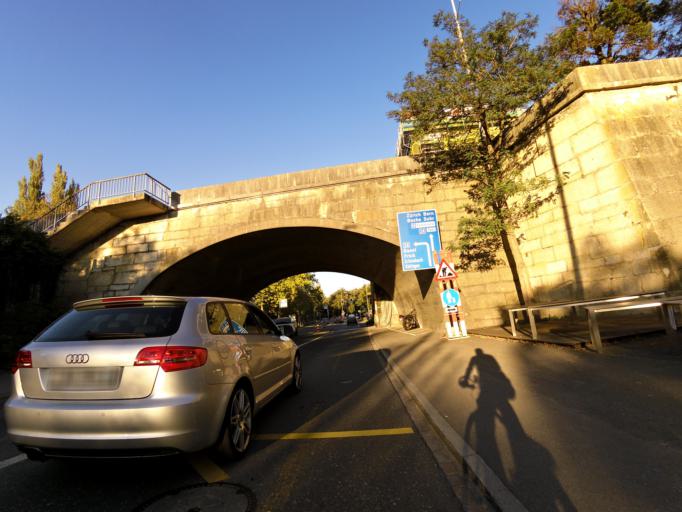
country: CH
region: Aargau
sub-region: Bezirk Aarau
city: Aarau
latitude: 47.3943
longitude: 8.0424
